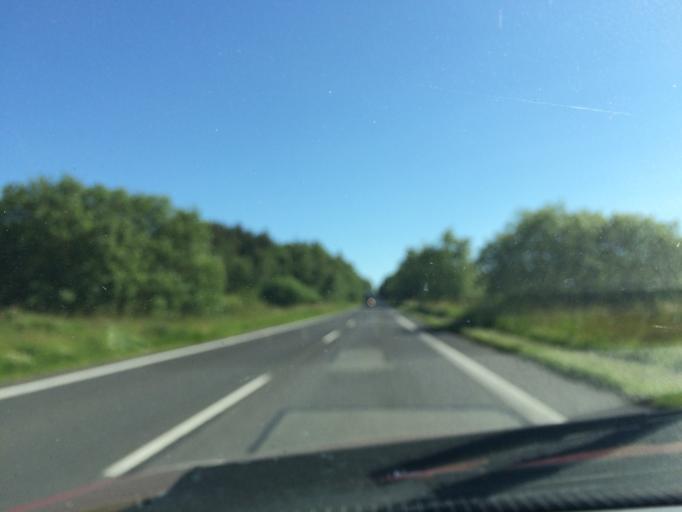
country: DK
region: Central Jutland
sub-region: Viborg Kommune
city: Bjerringbro
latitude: 56.3661
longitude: 9.6762
